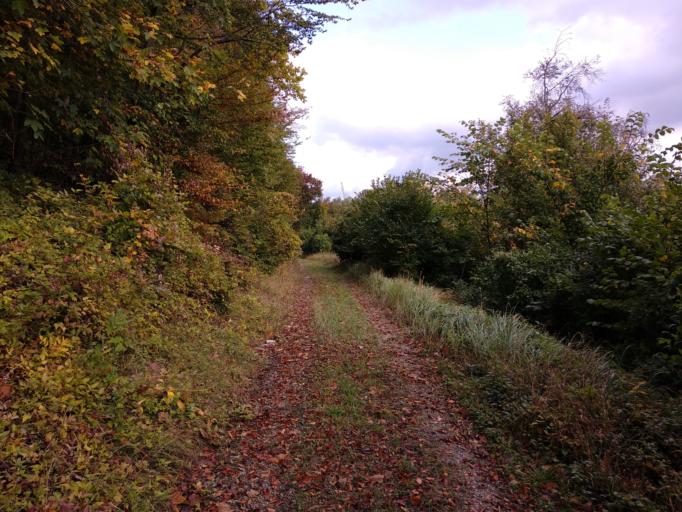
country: DE
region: North Rhine-Westphalia
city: Beverungen
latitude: 51.6418
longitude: 9.3673
